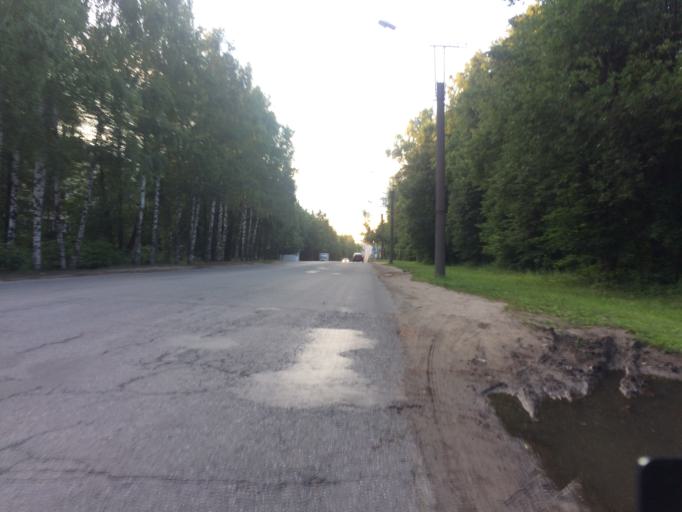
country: RU
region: Mariy-El
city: Yoshkar-Ola
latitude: 56.6246
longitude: 47.9540
